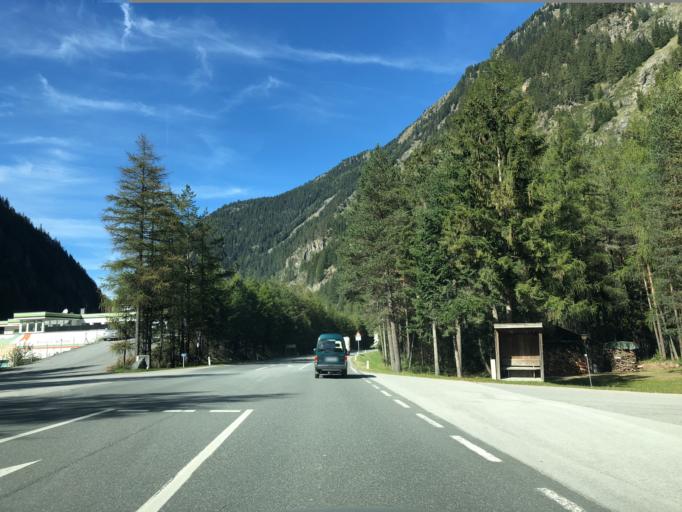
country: AT
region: Tyrol
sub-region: Politischer Bezirk Imst
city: Soelden
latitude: 47.0287
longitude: 10.9926
